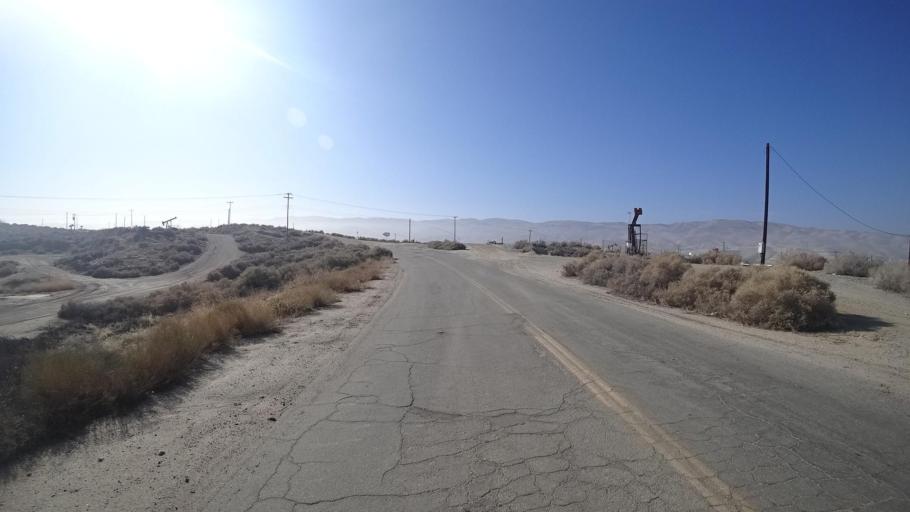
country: US
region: California
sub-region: Kern County
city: Taft Heights
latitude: 35.1187
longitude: -119.4782
